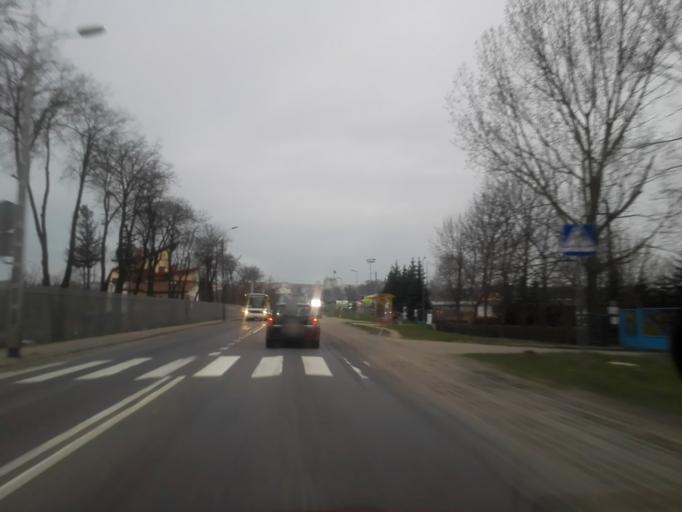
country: PL
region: Podlasie
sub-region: Powiat lomzynski
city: Piatnica
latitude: 53.1870
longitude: 22.0868
